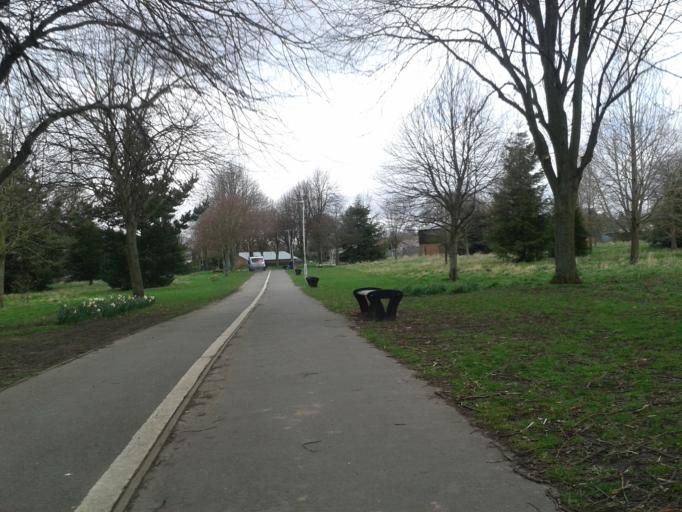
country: GB
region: England
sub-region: Leicestershire
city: Hinckley
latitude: 52.5407
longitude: -1.3846
